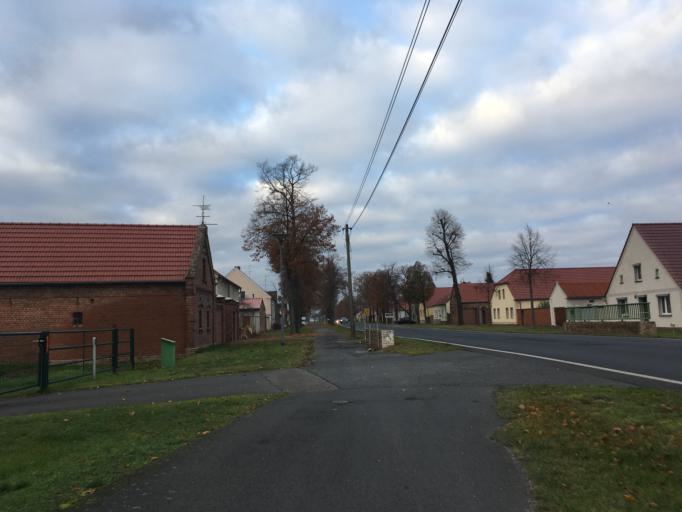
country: DE
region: Brandenburg
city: Neuhardenberg
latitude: 52.5922
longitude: 14.2611
